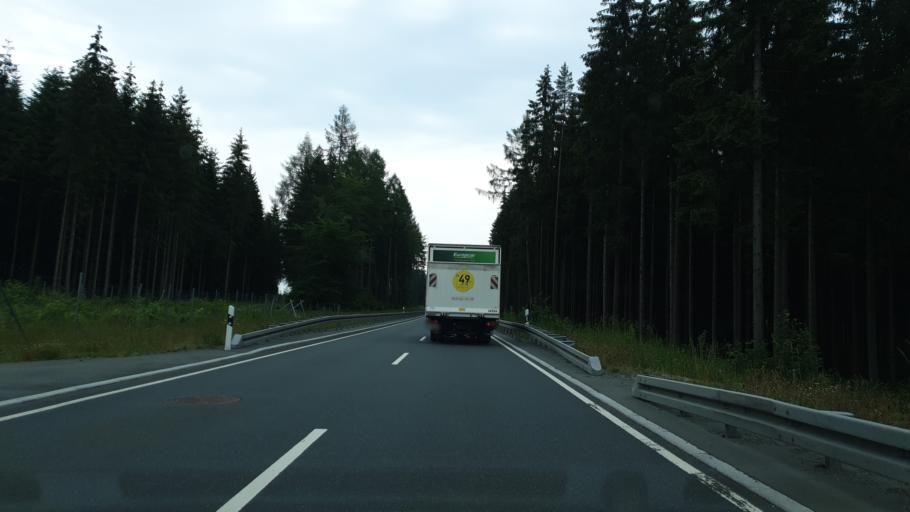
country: DE
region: Saxony
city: Tannenbergsthal
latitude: 50.4652
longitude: 12.4381
